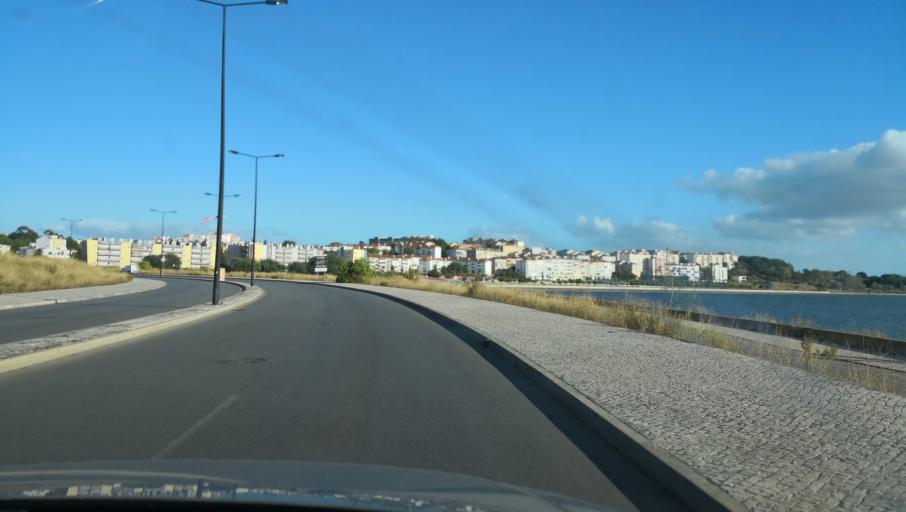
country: PT
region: Setubal
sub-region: Barreiro
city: Barreiro
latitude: 38.6504
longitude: -9.0698
